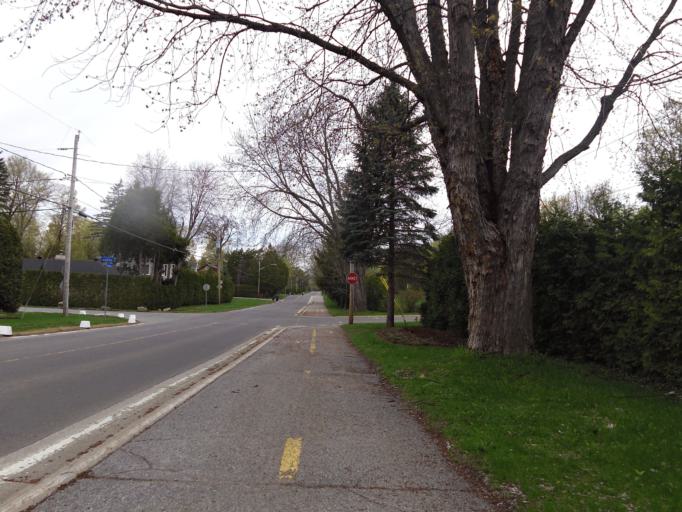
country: CA
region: Quebec
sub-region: Laurentides
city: Deux-Montagnes
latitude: 45.5259
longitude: -73.8755
